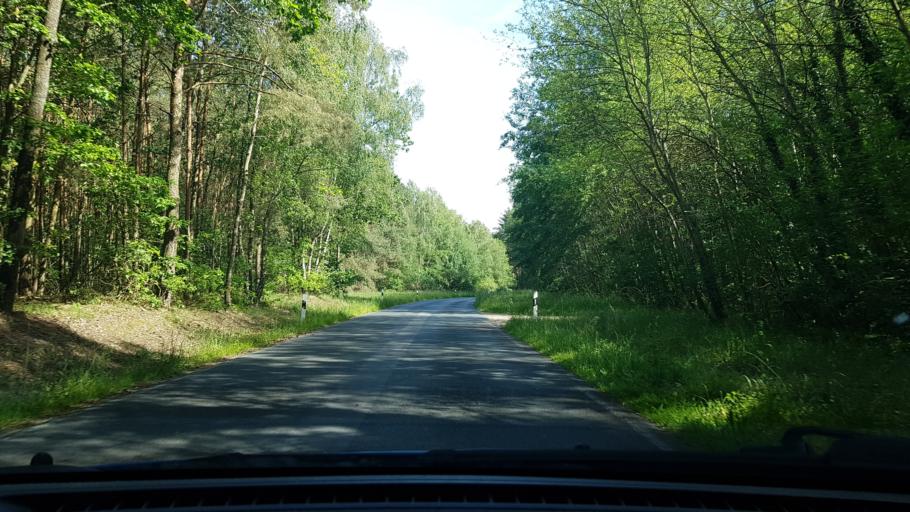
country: DE
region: Mecklenburg-Vorpommern
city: Boizenburg
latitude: 53.3534
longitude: 10.8404
